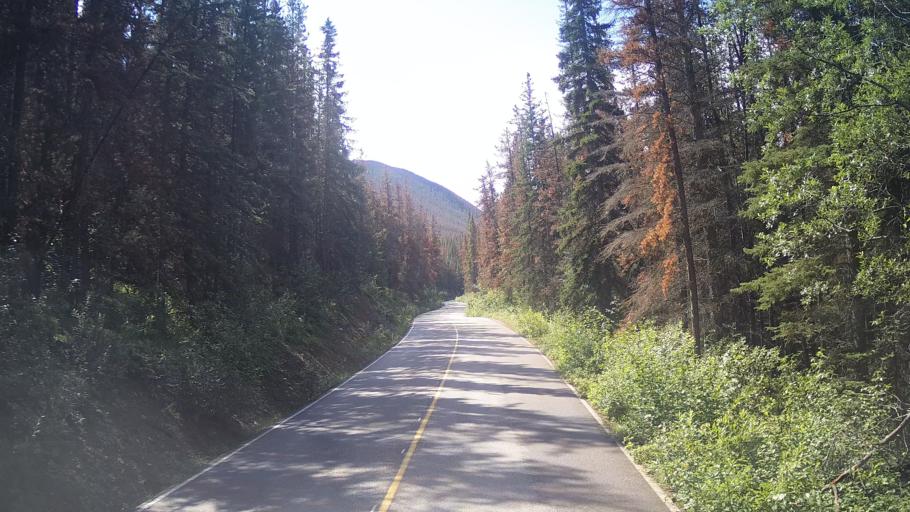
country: CA
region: Alberta
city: Jasper Park Lodge
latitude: 52.7687
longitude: -118.0369
